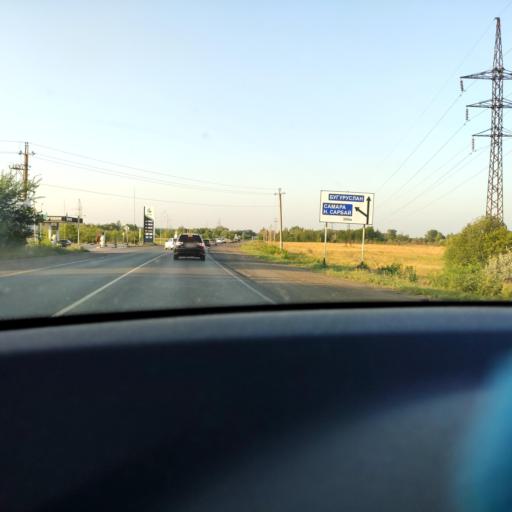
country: RU
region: Samara
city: Kinel'
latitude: 53.2452
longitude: 50.5854
